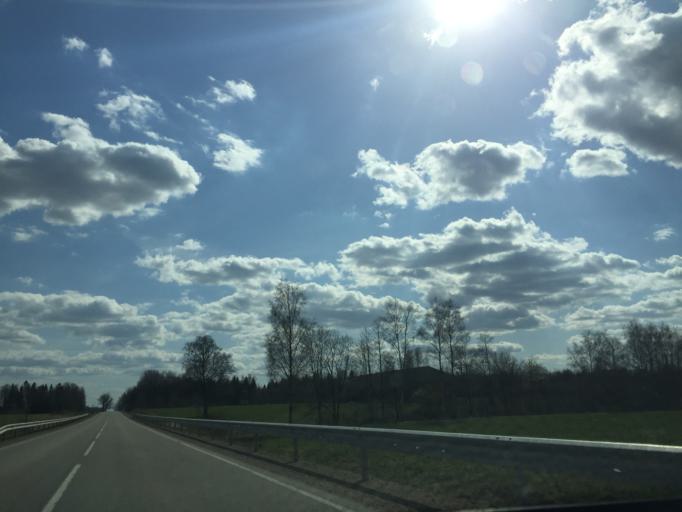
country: LV
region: Skriveri
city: Skriveri
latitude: 56.7473
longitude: 25.1671
